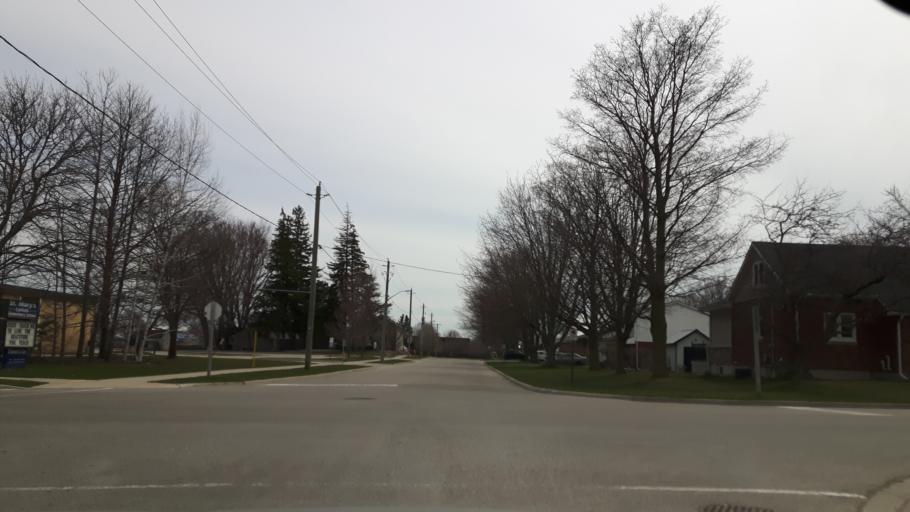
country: CA
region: Ontario
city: Goderich
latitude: 43.7338
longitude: -81.7086
